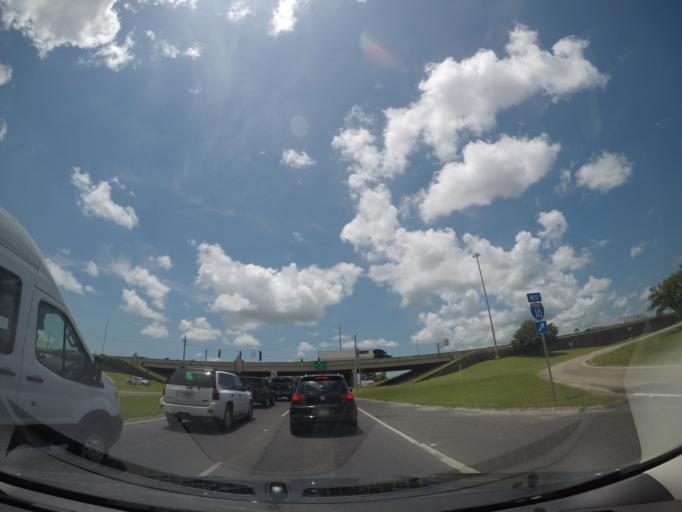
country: US
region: Louisiana
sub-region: Calcasieu Parish
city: Sulphur
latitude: 30.2167
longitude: -93.3764
